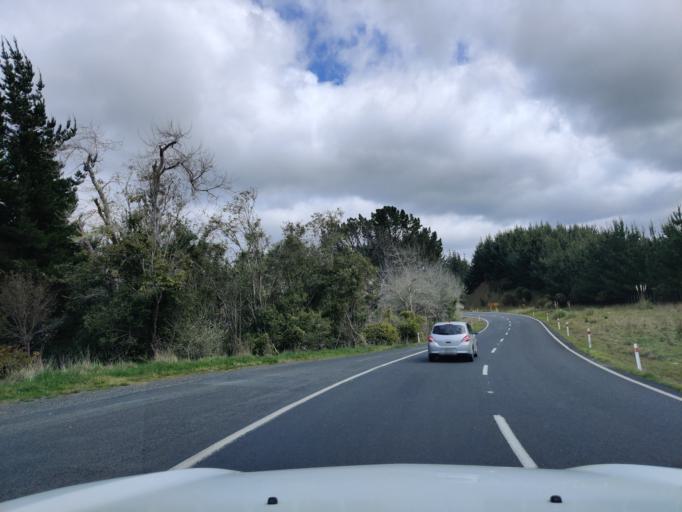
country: NZ
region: Manawatu-Wanganui
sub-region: Wanganui District
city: Wanganui
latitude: -39.7937
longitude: 175.2091
